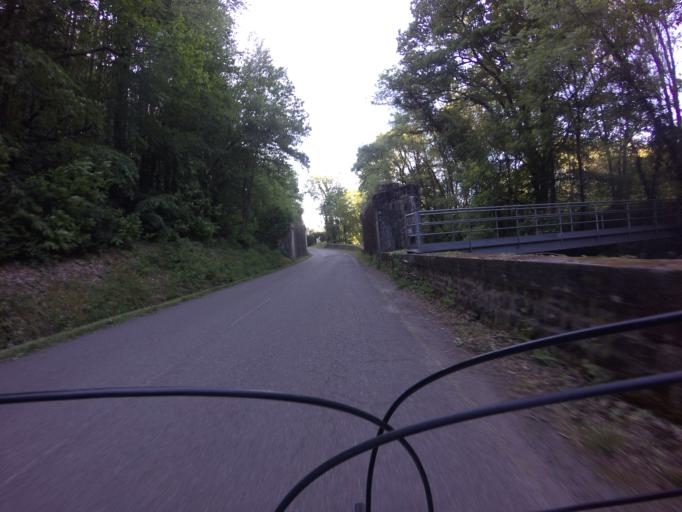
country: FR
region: Brittany
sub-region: Departement du Finistere
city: Quimper
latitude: 48.0269
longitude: -4.1466
